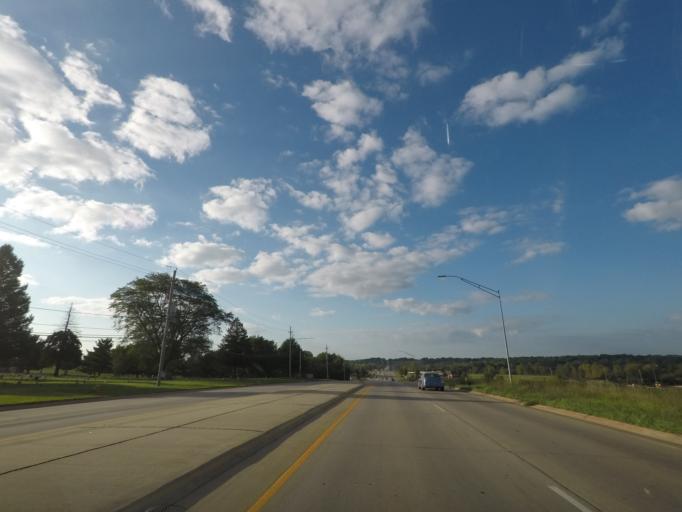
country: US
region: Iowa
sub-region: Warren County
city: Norwalk
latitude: 41.5151
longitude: -93.6451
